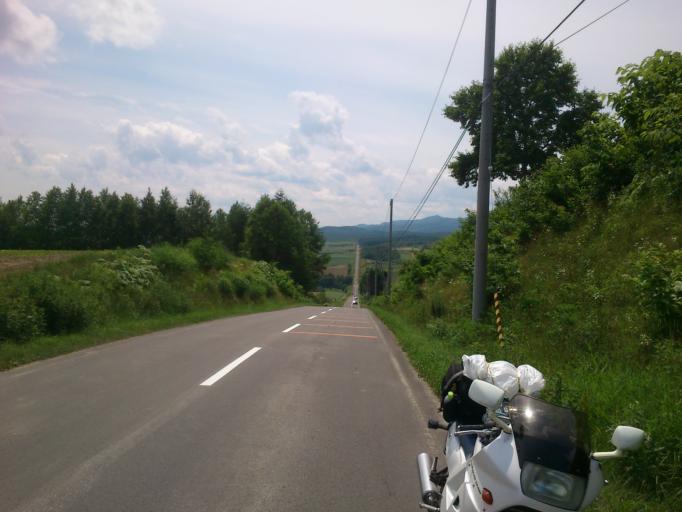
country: JP
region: Hokkaido
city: Shimo-furano
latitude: 43.5205
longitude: 142.4303
